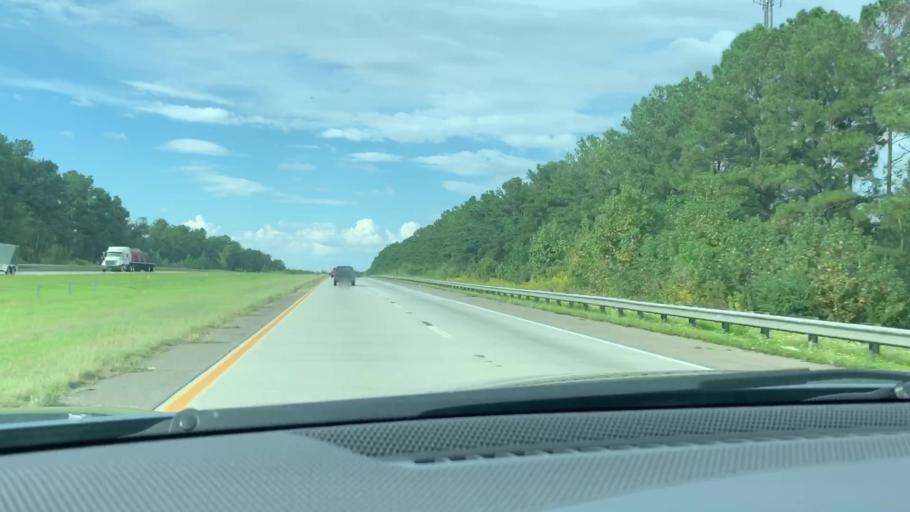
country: US
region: South Carolina
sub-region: Colleton County
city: Walterboro
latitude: 33.0326
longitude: -80.6675
